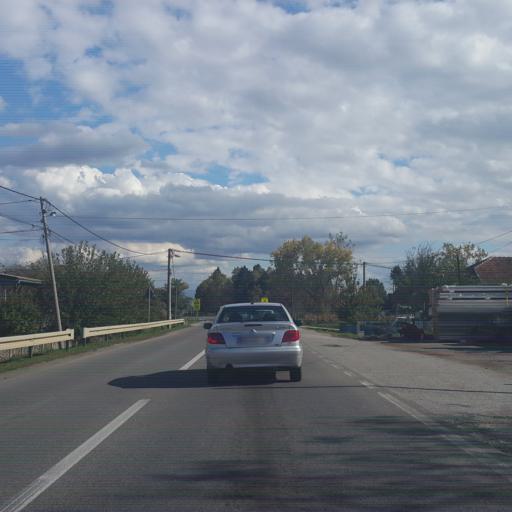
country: RS
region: Central Serbia
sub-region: Rasinski Okrug
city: Trstenik
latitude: 43.5917
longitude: 21.0683
